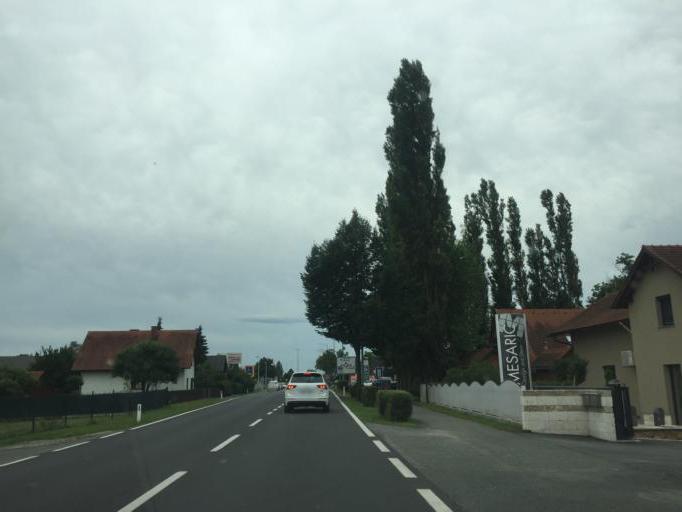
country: AT
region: Styria
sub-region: Politischer Bezirk Leibnitz
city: Kaindorf an der Sulm
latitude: 46.8051
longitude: 15.5532
